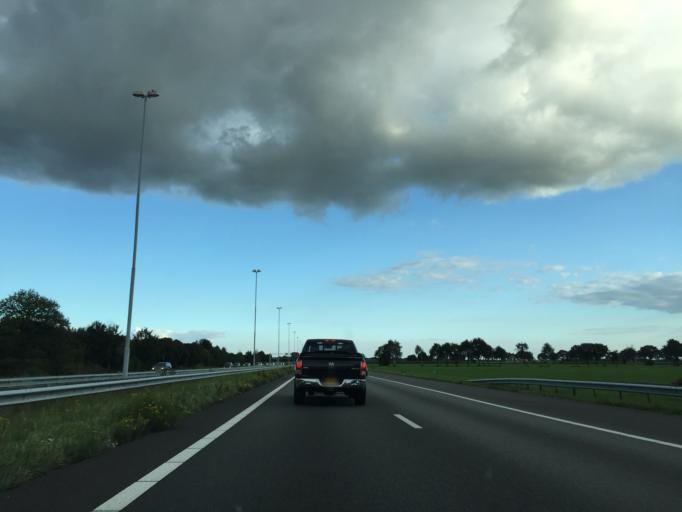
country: NL
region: North Brabant
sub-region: Gemeente Dongen
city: Dongen
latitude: 51.5451
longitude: 4.9785
